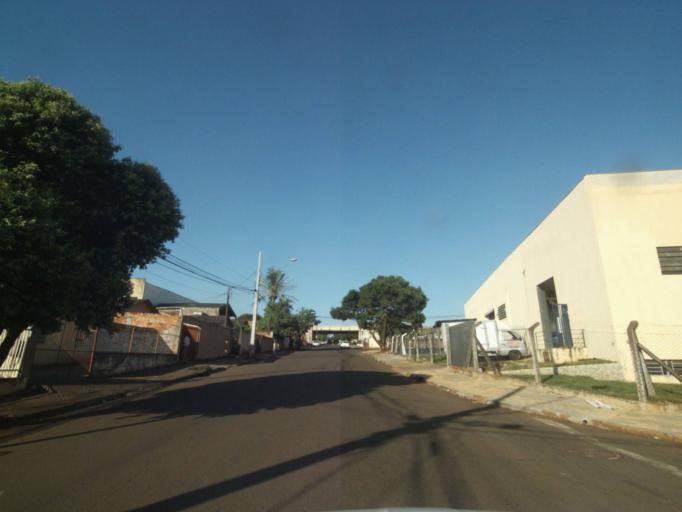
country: BR
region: Parana
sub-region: Cambe
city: Cambe
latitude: -23.3053
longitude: -51.2250
